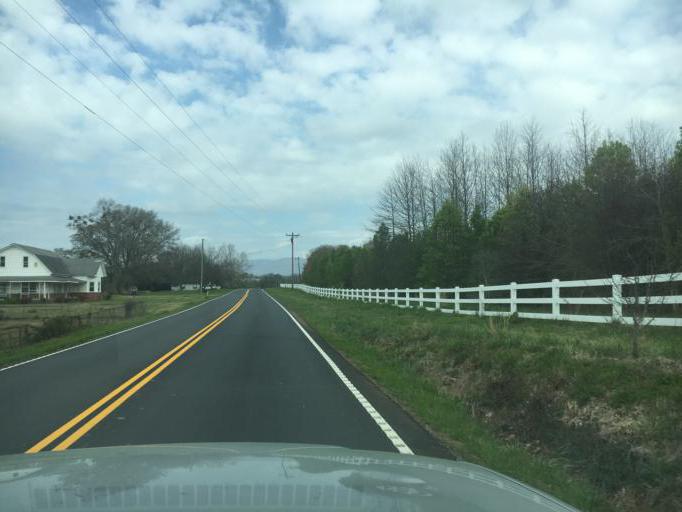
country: US
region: South Carolina
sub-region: Spartanburg County
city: Landrum
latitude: 35.0869
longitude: -82.1936
